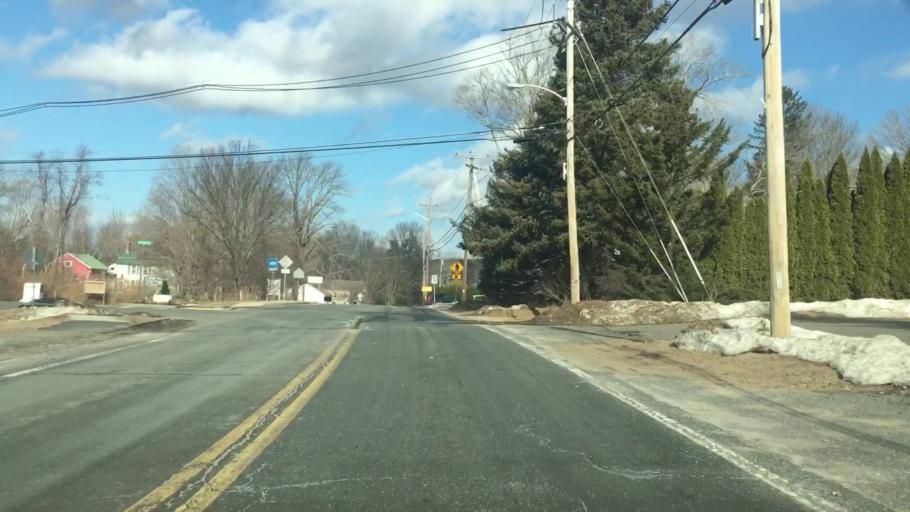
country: US
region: Massachusetts
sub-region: Hampden County
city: Wales
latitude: 42.0676
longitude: -72.2223
